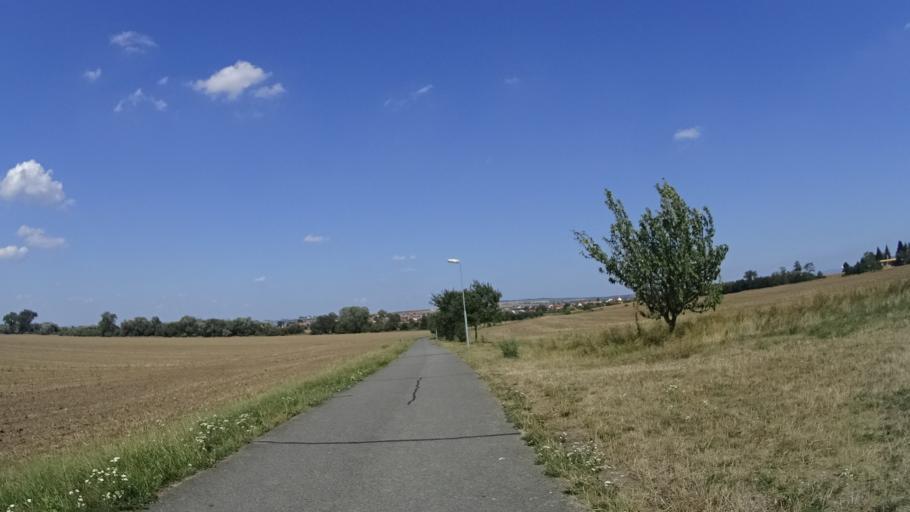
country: CZ
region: Zlin
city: Uhersky Ostroh
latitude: 48.9925
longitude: 17.4123
